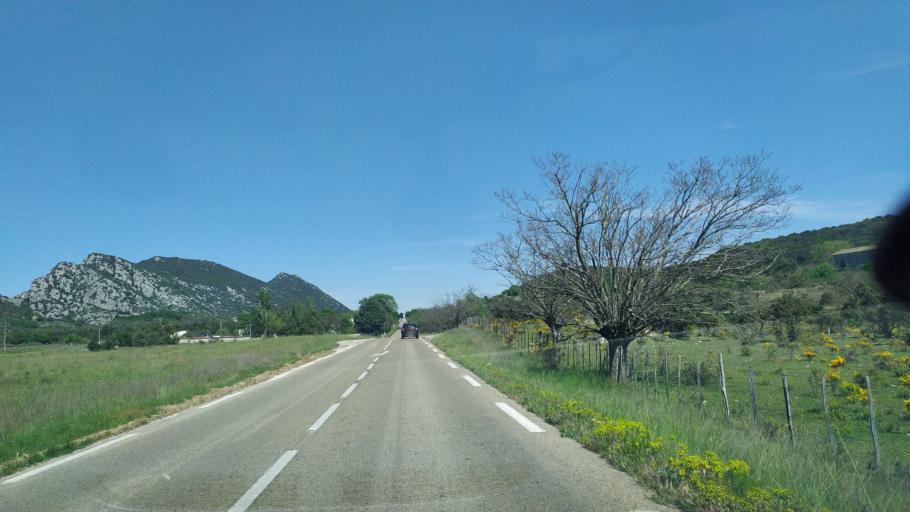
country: FR
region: Languedoc-Roussillon
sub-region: Departement du Gard
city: Saint-Hippolyte-du-Fort
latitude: 43.9492
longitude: 3.7909
